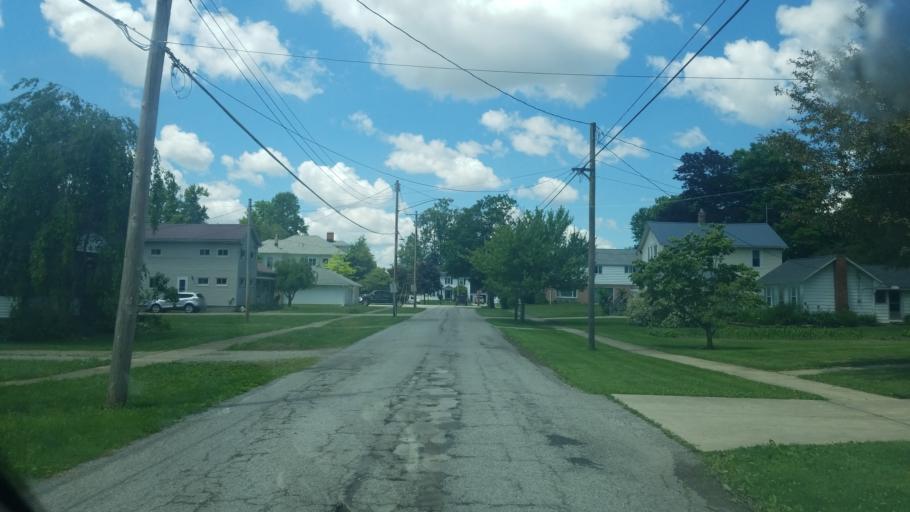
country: US
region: Ohio
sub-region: Huron County
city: New London
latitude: 41.0797
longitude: -82.3956
